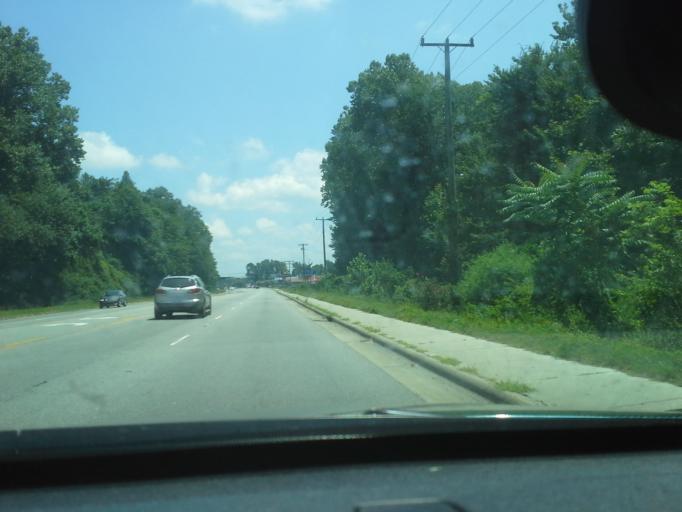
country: US
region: North Carolina
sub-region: Washington County
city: Plymouth
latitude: 35.8593
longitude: -76.7421
